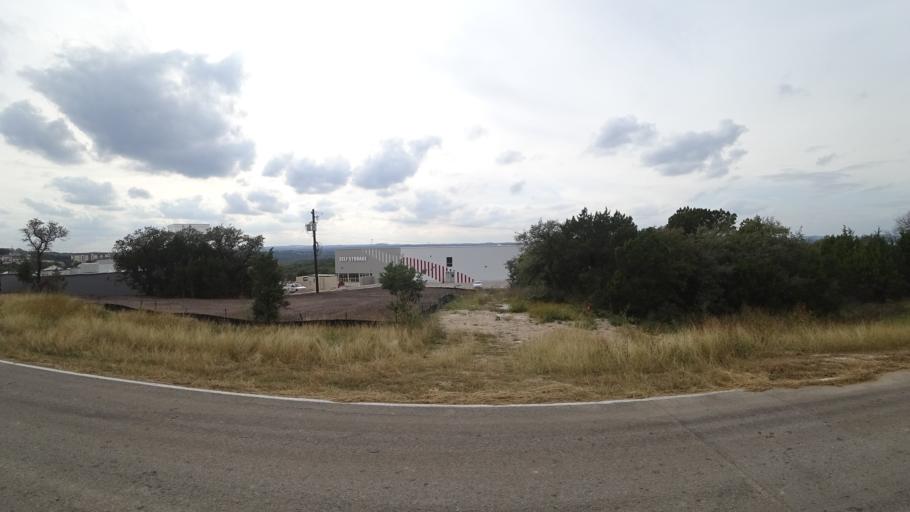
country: US
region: Texas
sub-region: Travis County
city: Hudson Bend
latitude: 30.3918
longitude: -97.8847
